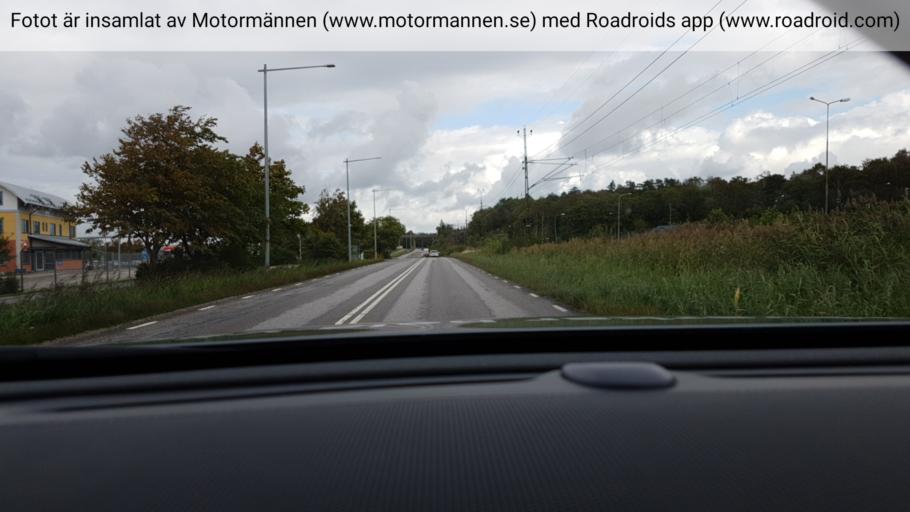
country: SE
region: Vaestra Goetaland
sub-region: Stenungsunds Kommun
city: Stenungsund
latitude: 58.0894
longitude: 11.8317
